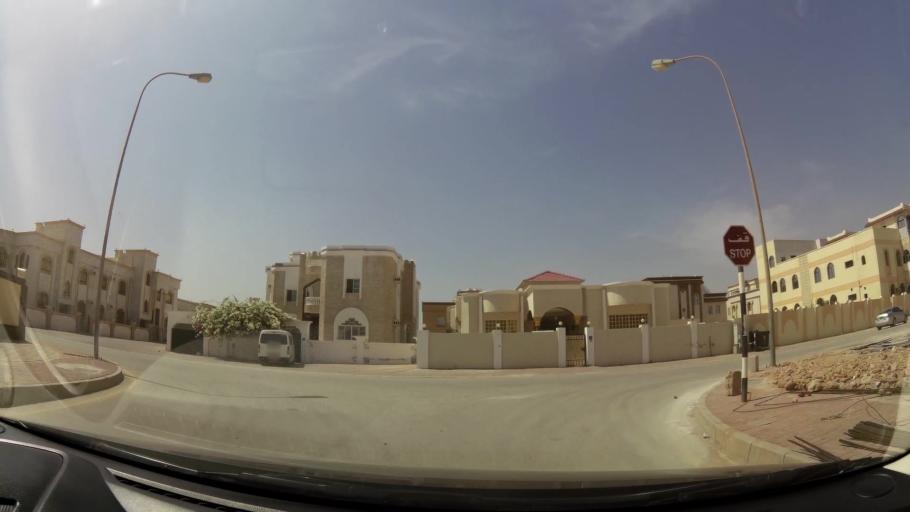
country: OM
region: Zufar
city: Salalah
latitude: 17.0415
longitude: 54.1529
